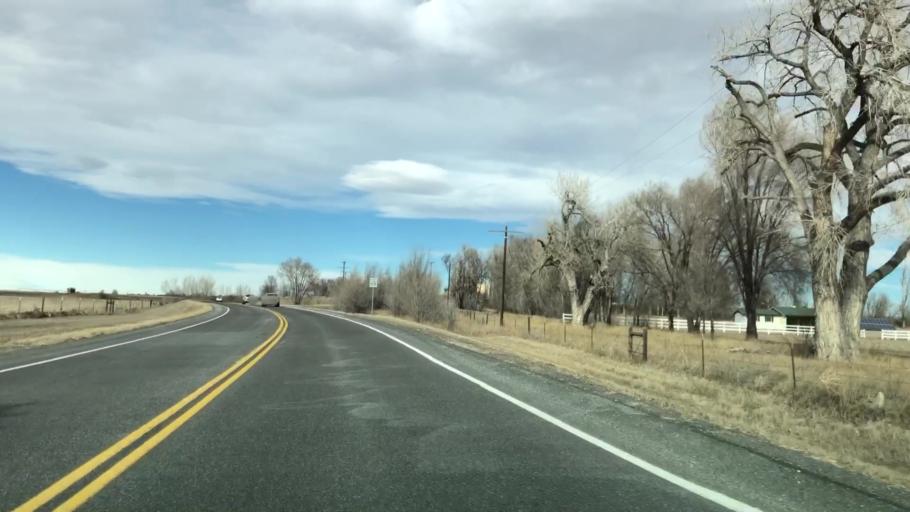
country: US
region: Colorado
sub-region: Weld County
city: Windsor
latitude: 40.5088
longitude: -104.9266
